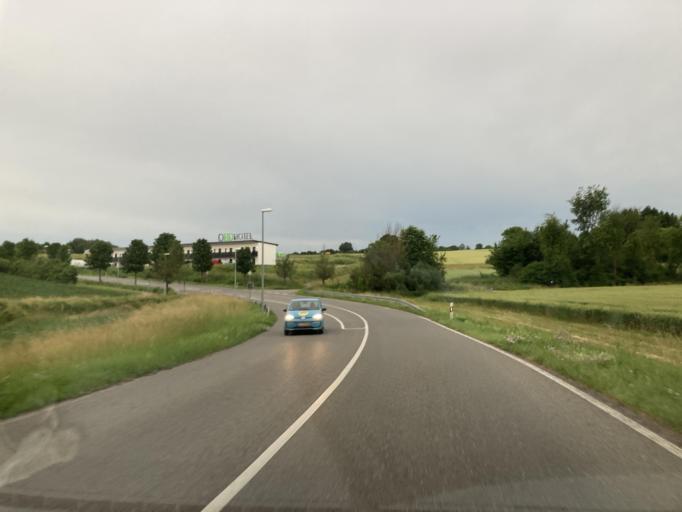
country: DE
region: Baden-Wuerttemberg
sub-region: Karlsruhe Region
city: Oberderdingen
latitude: 49.0845
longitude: 8.7671
